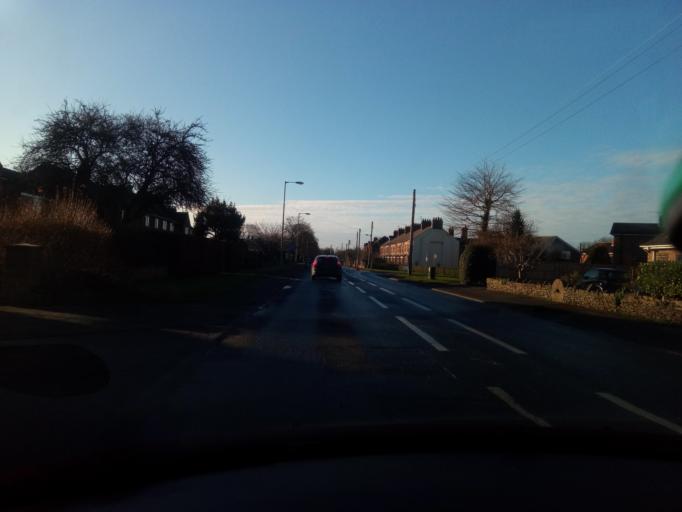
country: GB
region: England
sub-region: North Yorkshire
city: Thirsk
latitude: 54.2277
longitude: -1.3765
